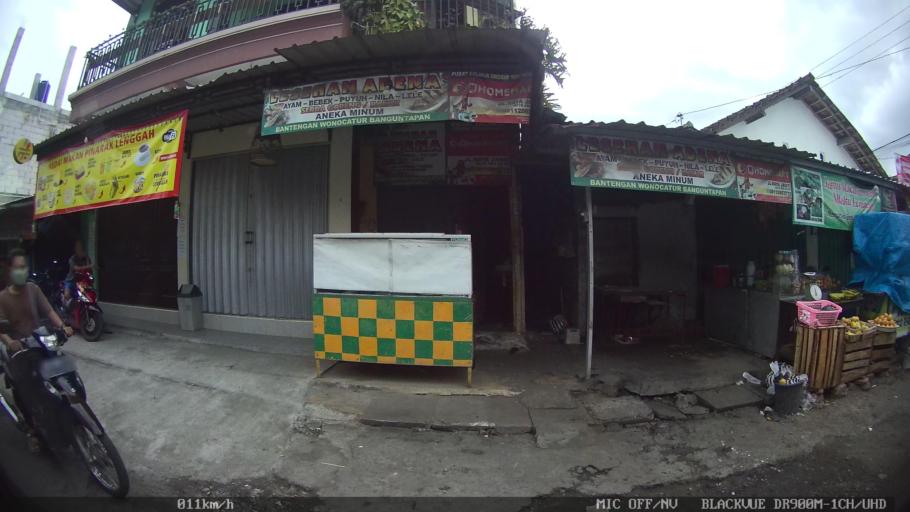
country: ID
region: Daerah Istimewa Yogyakarta
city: Depok
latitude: -7.8026
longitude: 110.4119
